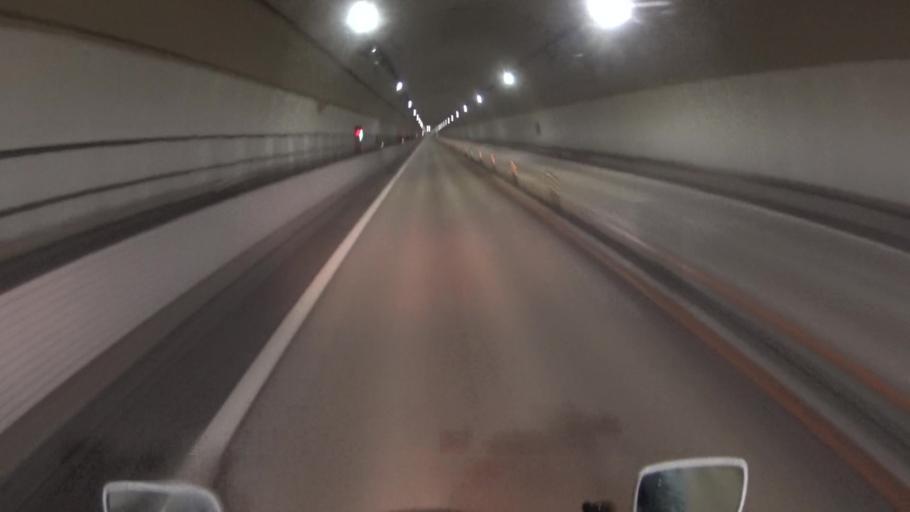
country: JP
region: Kyoto
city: Ayabe
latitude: 35.4046
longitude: 135.2292
